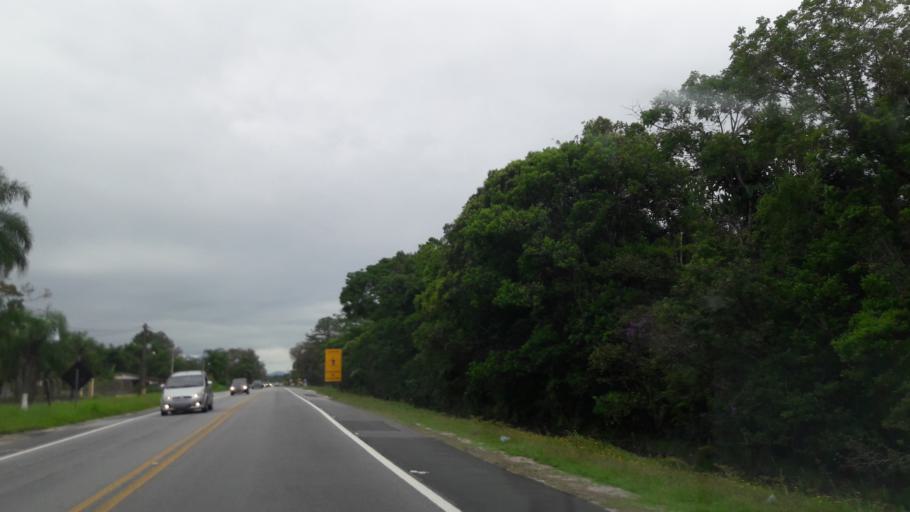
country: BR
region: Parana
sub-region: Pontal Do Parana
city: Pontal do Parana
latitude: -25.6757
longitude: -48.5071
